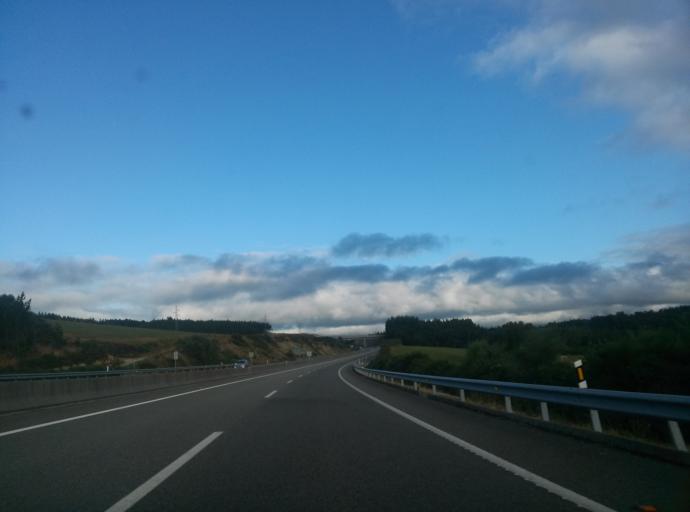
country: ES
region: Galicia
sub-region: Provincia de Lugo
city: Vilalba
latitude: 43.3507
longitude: -7.7378
